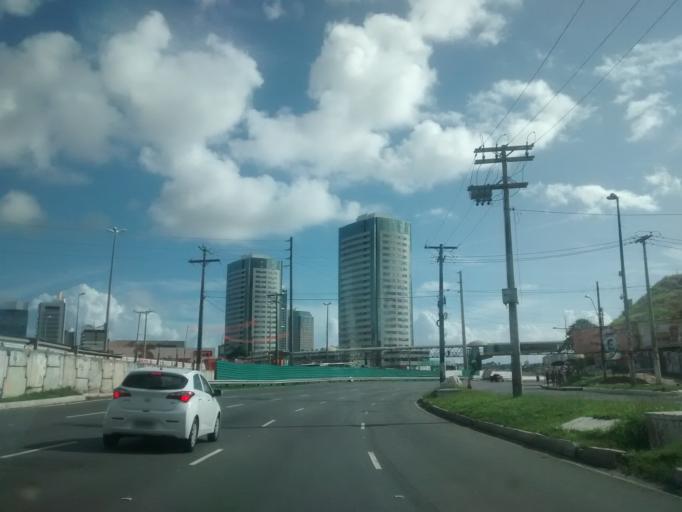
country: BR
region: Bahia
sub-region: Salvador
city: Salvador
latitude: -12.9755
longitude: -38.4534
